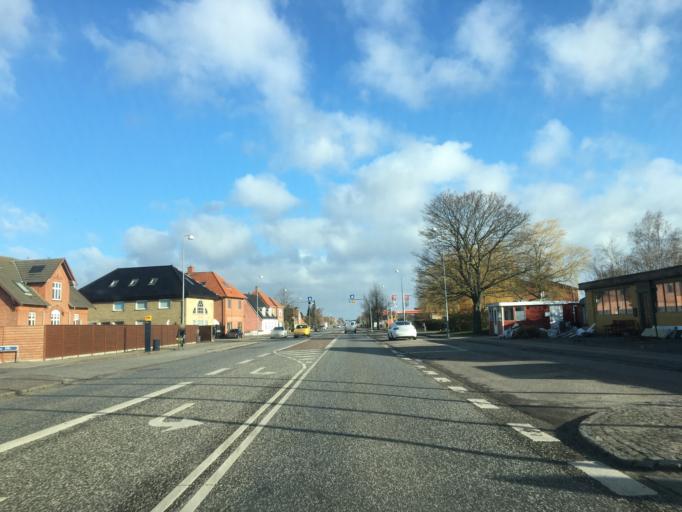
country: DK
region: Capital Region
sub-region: Tarnby Kommune
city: Tarnby
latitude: 55.6254
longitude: 12.6247
